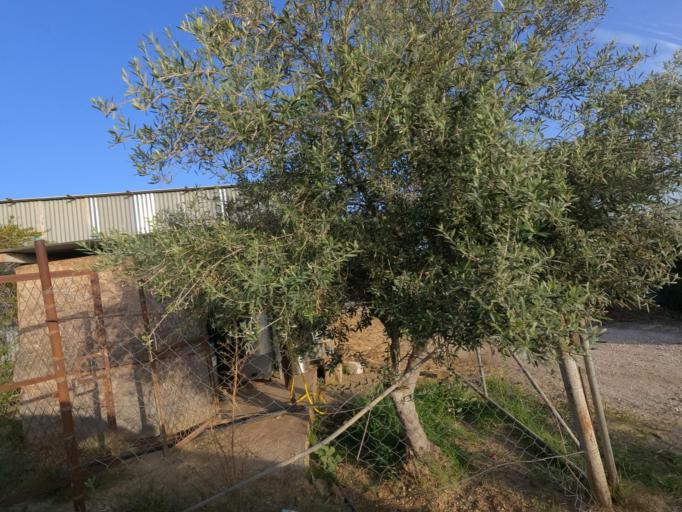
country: CY
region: Lefkosia
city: Astromeritis
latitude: 35.0763
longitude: 33.0206
